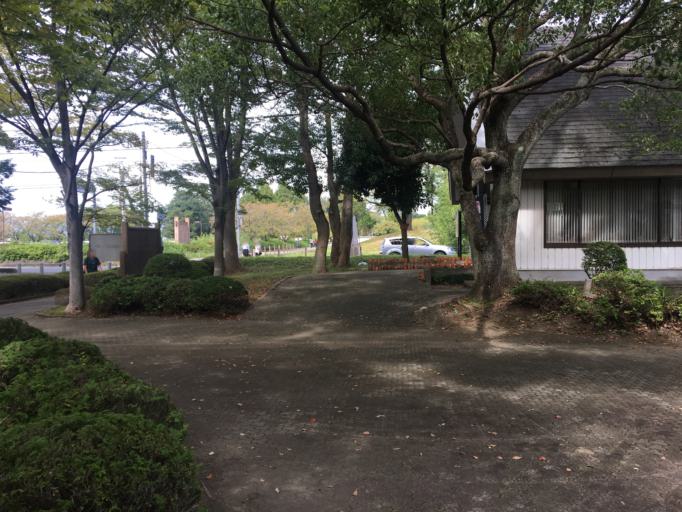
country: JP
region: Saitama
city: Gyoda
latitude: 36.1255
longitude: 139.4765
